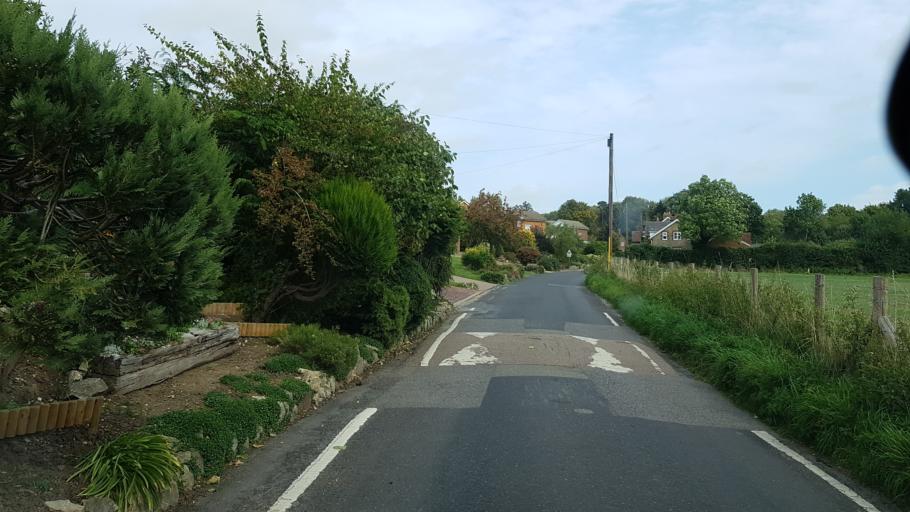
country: GB
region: England
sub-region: Kent
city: Meopham
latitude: 51.3161
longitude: 0.3540
